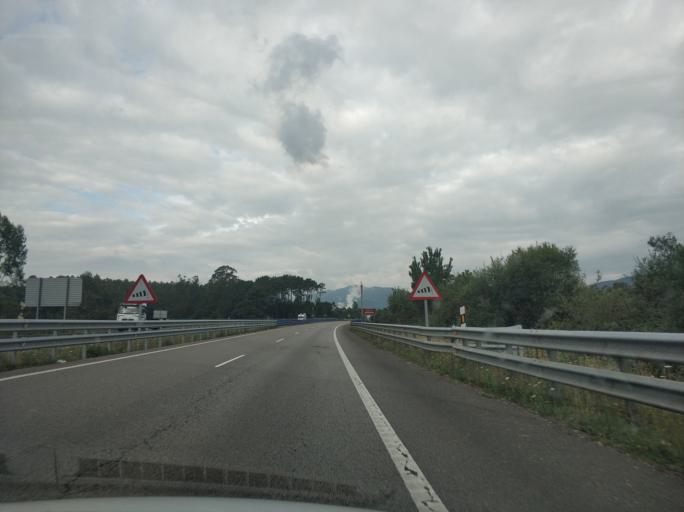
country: ES
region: Asturias
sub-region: Province of Asturias
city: Navia
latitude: 43.5310
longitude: -6.7084
